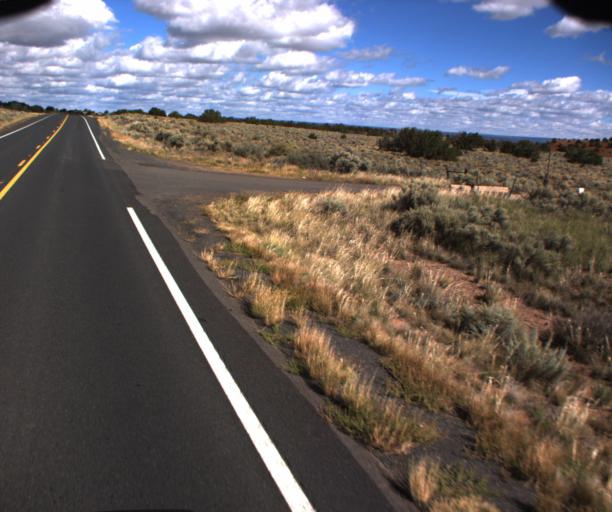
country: US
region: Arizona
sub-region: Apache County
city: Houck
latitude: 35.1651
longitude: -109.3376
